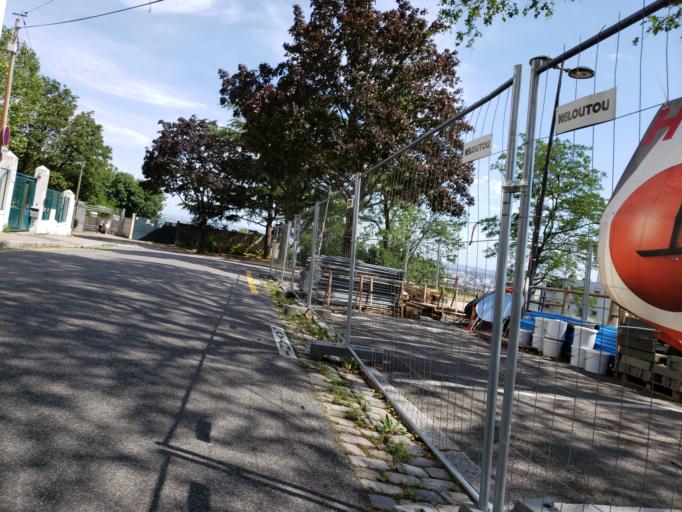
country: FR
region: Rhone-Alpes
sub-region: Departement du Rhone
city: Lyon
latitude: 45.7551
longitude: 4.8205
